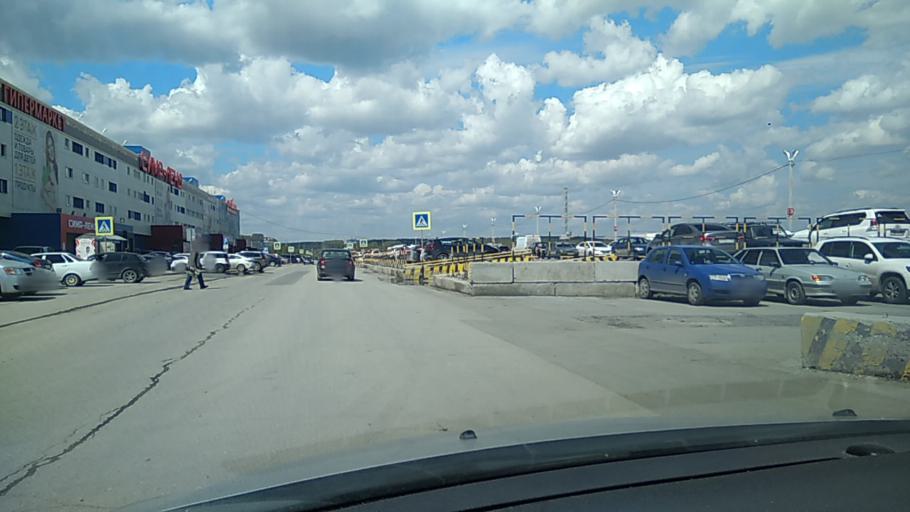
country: RU
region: Sverdlovsk
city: Istok
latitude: 56.7610
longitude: 60.7520
